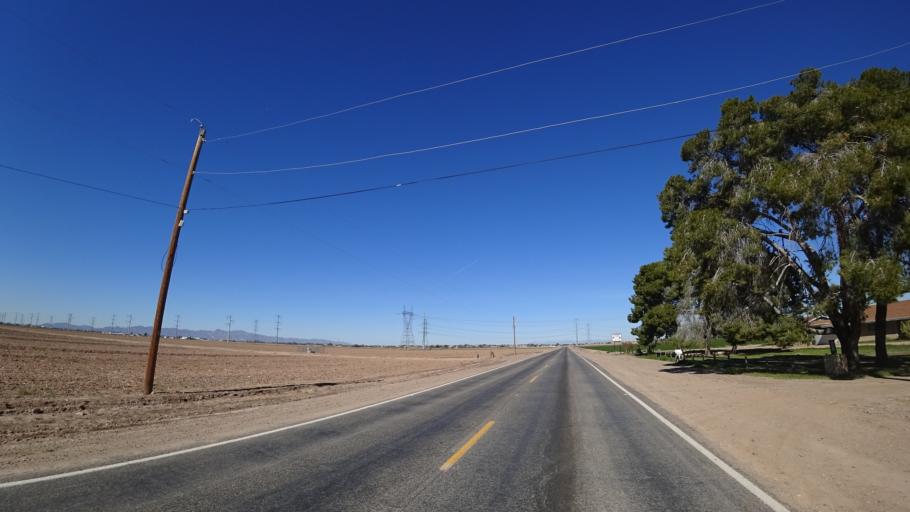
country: US
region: Arizona
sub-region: Maricopa County
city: Avondale
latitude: 33.3981
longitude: -112.3233
